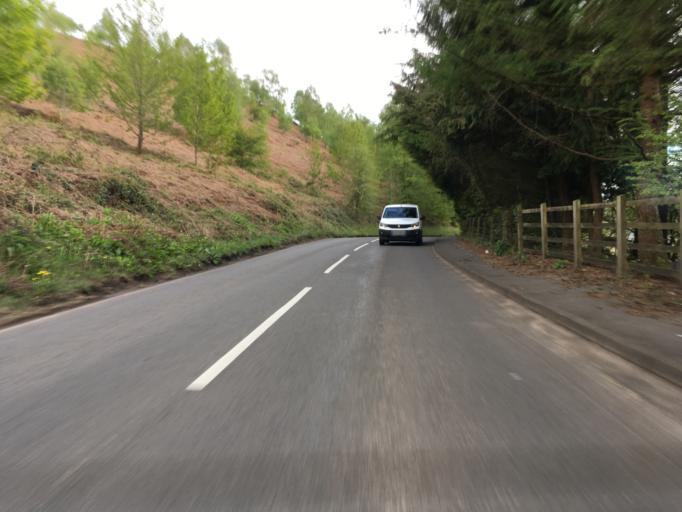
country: GB
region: Wales
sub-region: Merthyr Tydfil County Borough
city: Treharris
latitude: 51.6798
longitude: -3.2954
